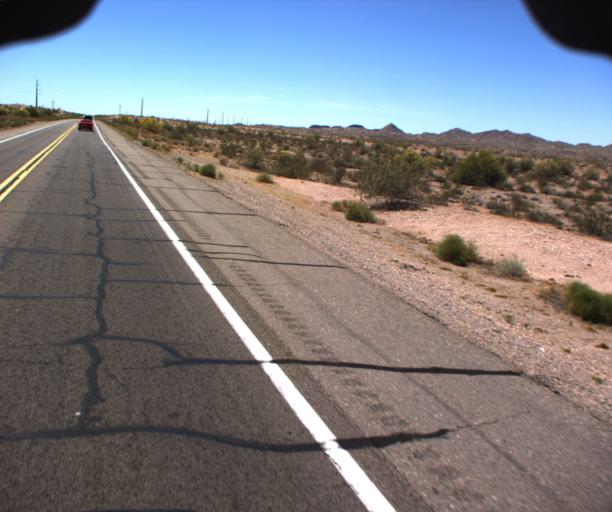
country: US
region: Arizona
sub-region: Mohave County
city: Desert Hills
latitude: 34.6694
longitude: -114.3112
